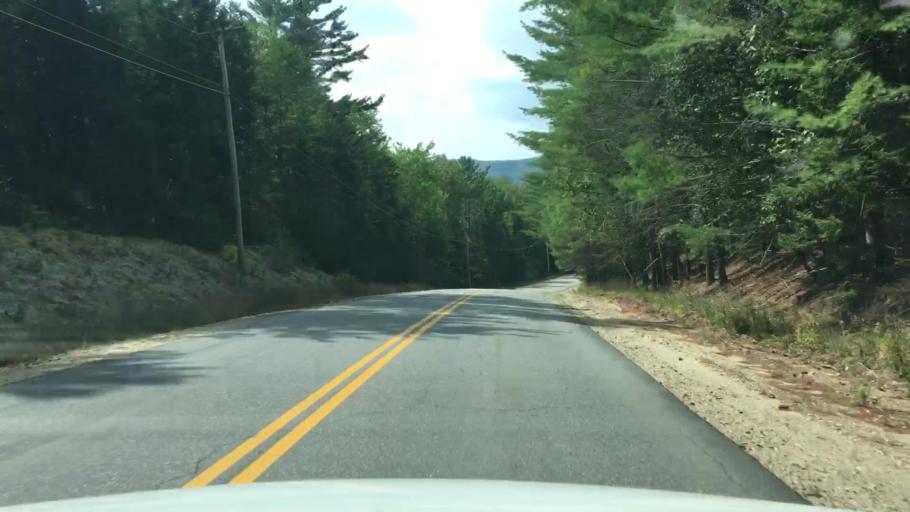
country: US
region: Maine
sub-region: Oxford County
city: Rumford
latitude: 44.5306
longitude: -70.6590
